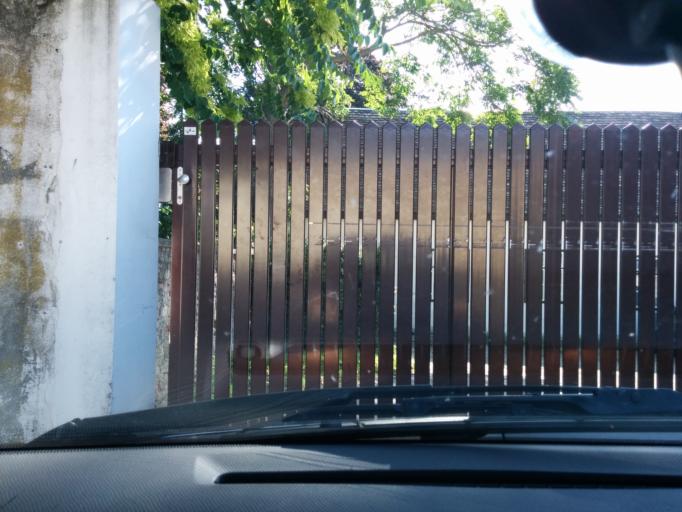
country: AT
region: Lower Austria
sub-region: Politischer Bezirk Modling
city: Modling
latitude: 48.0867
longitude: 16.2854
